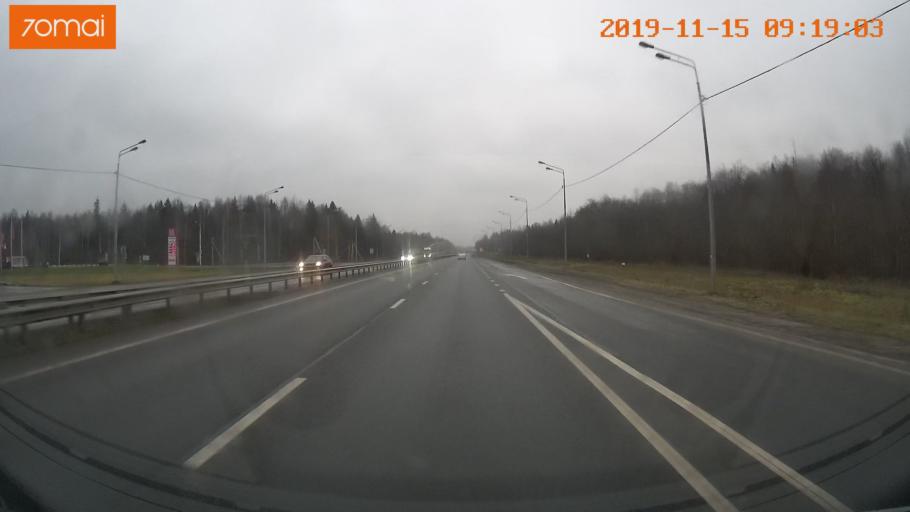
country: RU
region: Vologda
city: Tonshalovo
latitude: 59.2805
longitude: 38.0086
